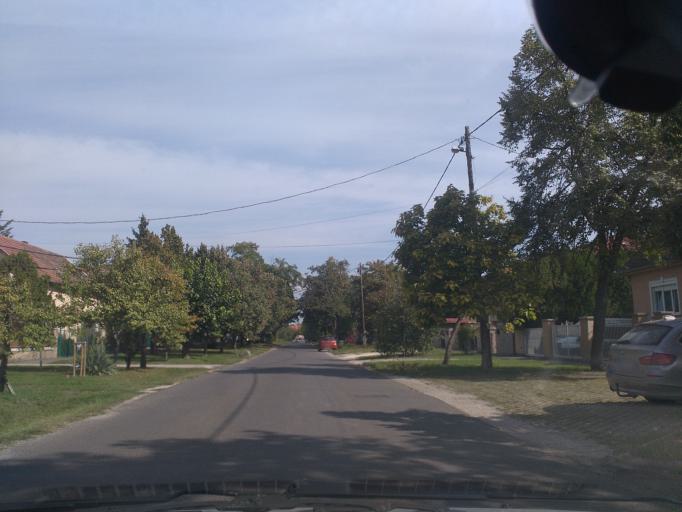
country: HU
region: Pest
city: Gyal
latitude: 47.4237
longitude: 19.2214
